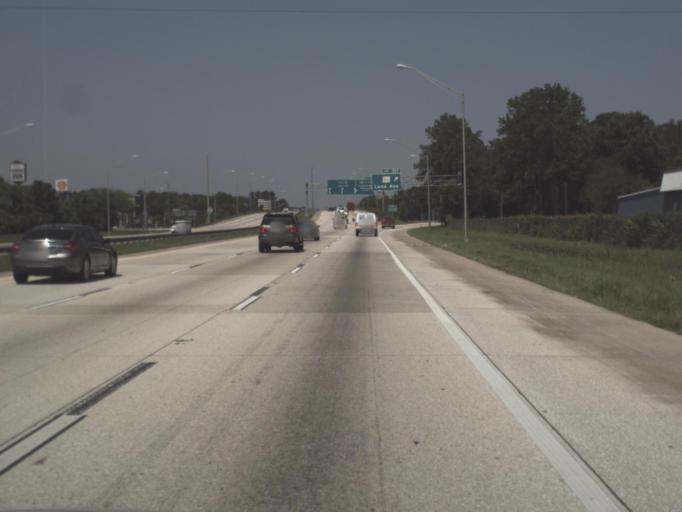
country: US
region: Florida
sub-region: Duval County
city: Jacksonville
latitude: 30.3157
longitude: -81.7473
